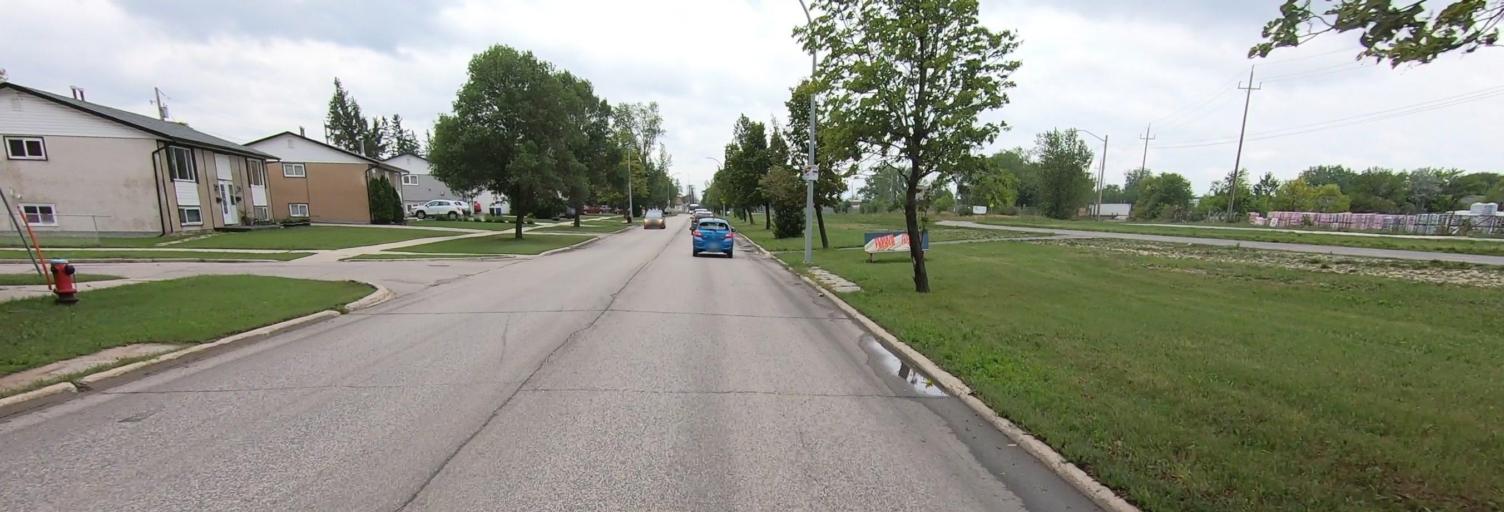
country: CA
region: Manitoba
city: Winnipeg
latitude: 49.9129
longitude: -97.0914
